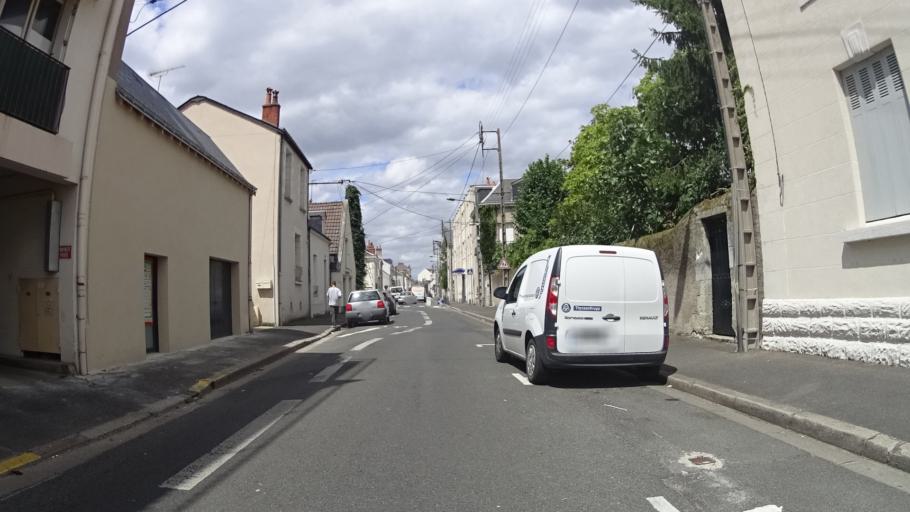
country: FR
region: Centre
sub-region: Departement d'Indre-et-Loire
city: Tours
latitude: 47.3805
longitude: 0.6797
